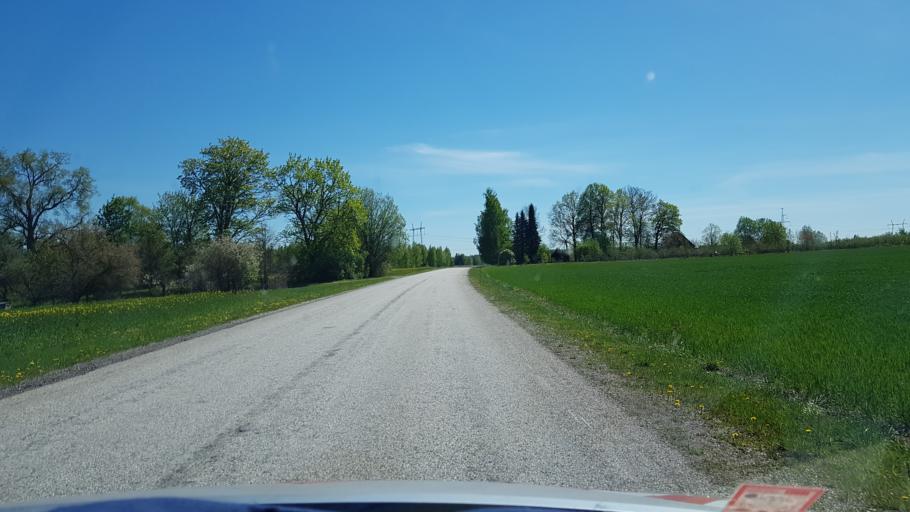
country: EE
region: Tartu
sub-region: UElenurme vald
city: Ulenurme
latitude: 58.2796
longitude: 26.9055
